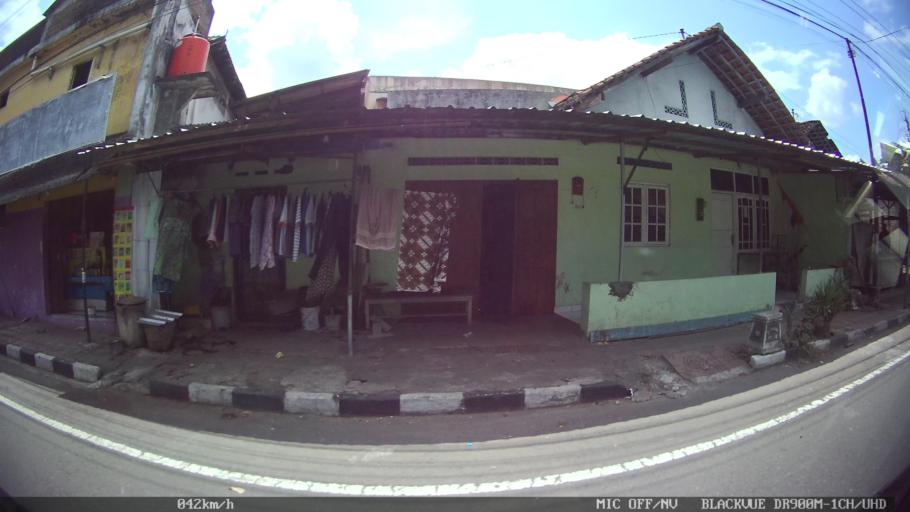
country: ID
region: Daerah Istimewa Yogyakarta
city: Bantul
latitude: -7.8920
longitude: 110.3306
